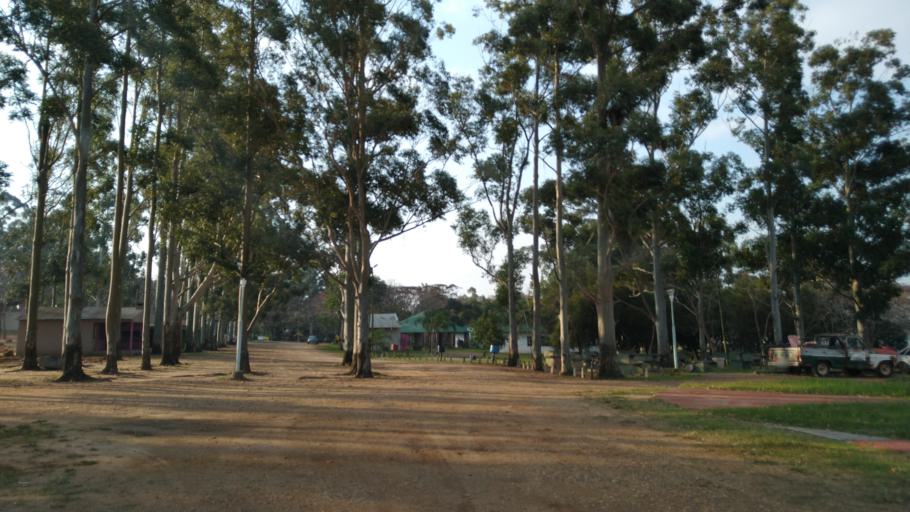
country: AR
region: Entre Rios
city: Santa Ana
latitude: -30.9143
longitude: -57.9261
